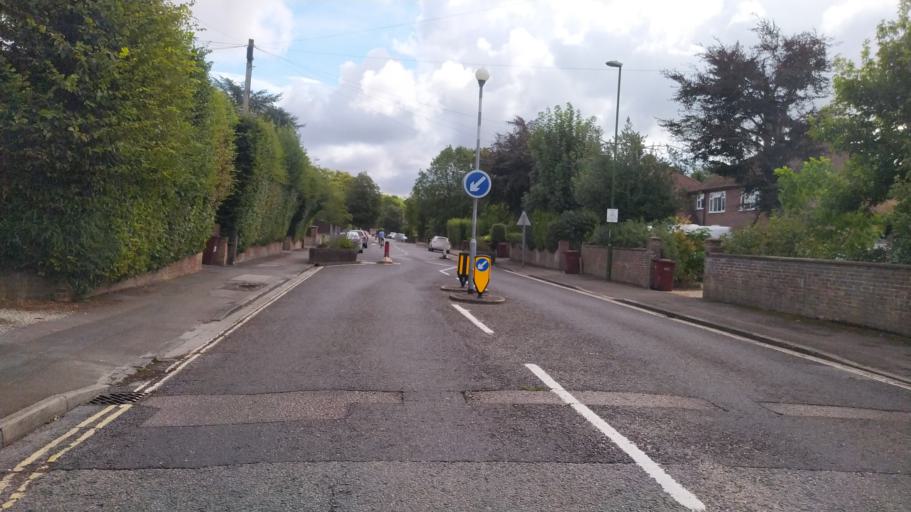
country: GB
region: England
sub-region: West Sussex
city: Chichester
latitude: 50.8359
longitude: -0.7933
